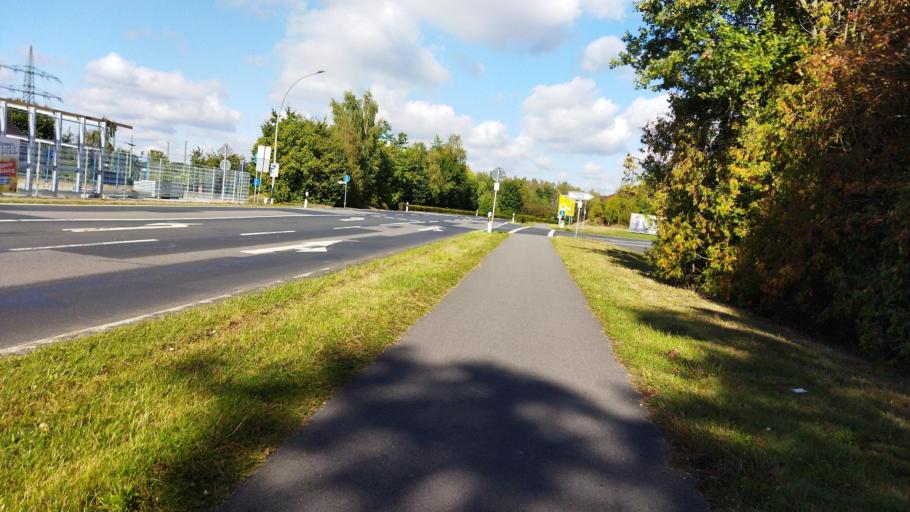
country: DE
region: Lower Saxony
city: Salzbergen
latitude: 52.3276
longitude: 7.3471
